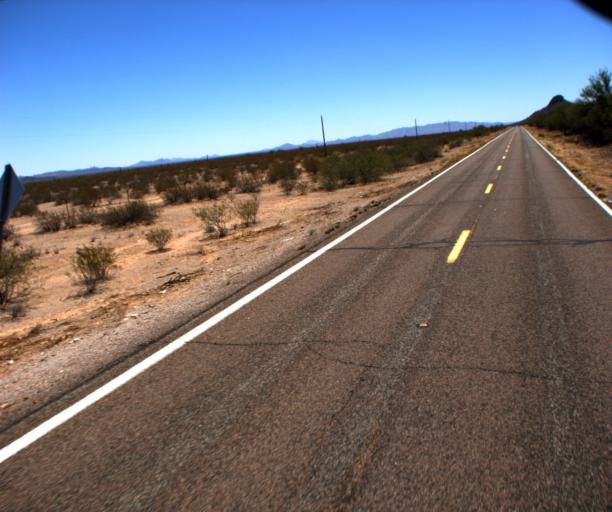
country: US
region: Arizona
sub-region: Pima County
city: Ajo
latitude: 32.2056
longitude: -112.5625
